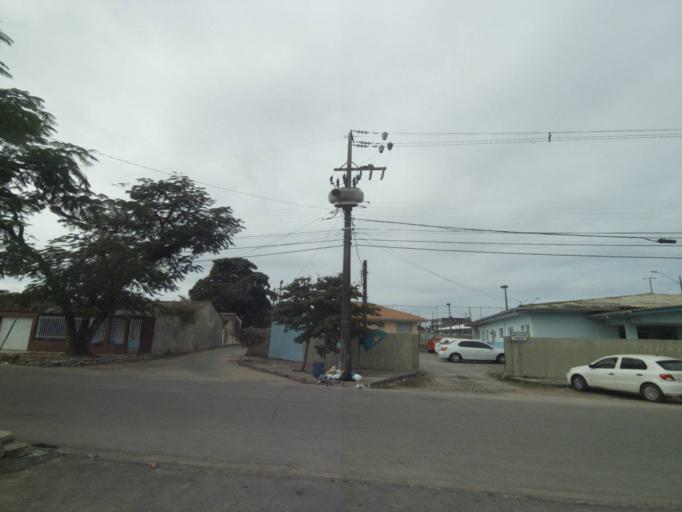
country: BR
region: Parana
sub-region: Paranagua
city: Paranagua
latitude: -25.5157
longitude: -48.5312
